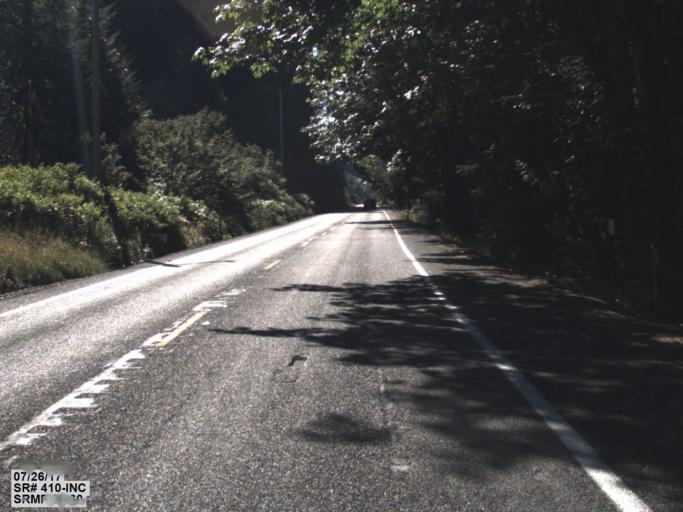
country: US
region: Washington
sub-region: King County
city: Enumclaw
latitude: 47.1736
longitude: -121.7761
